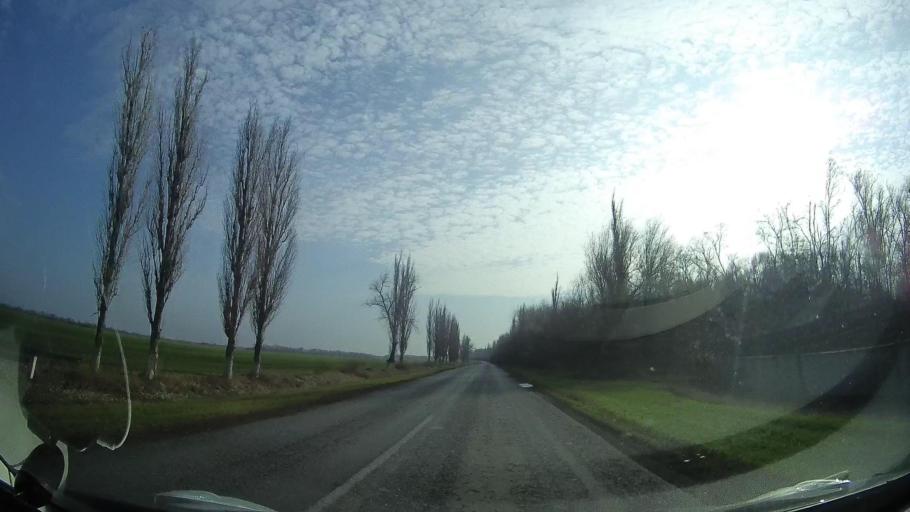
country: RU
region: Rostov
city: Mechetinskaya
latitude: 46.8272
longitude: 40.5526
